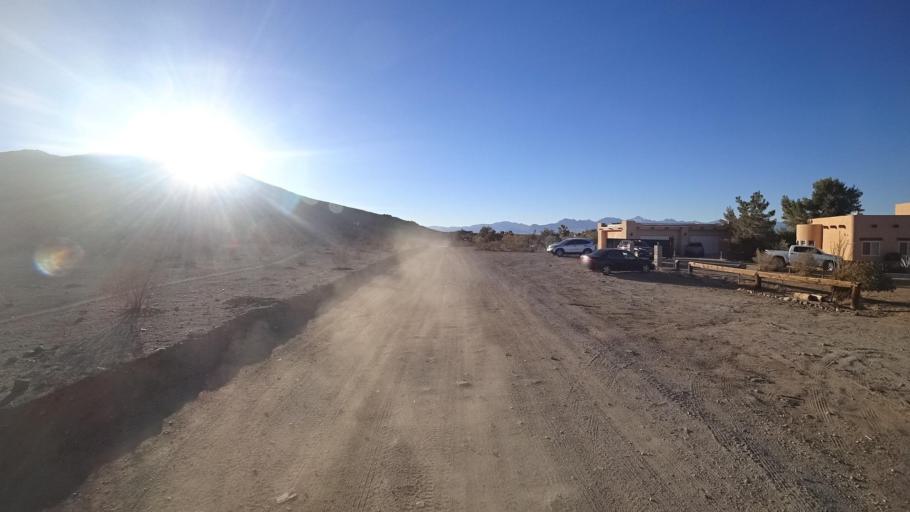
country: US
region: California
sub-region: Kern County
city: Ridgecrest
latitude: 35.5788
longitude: -117.6538
